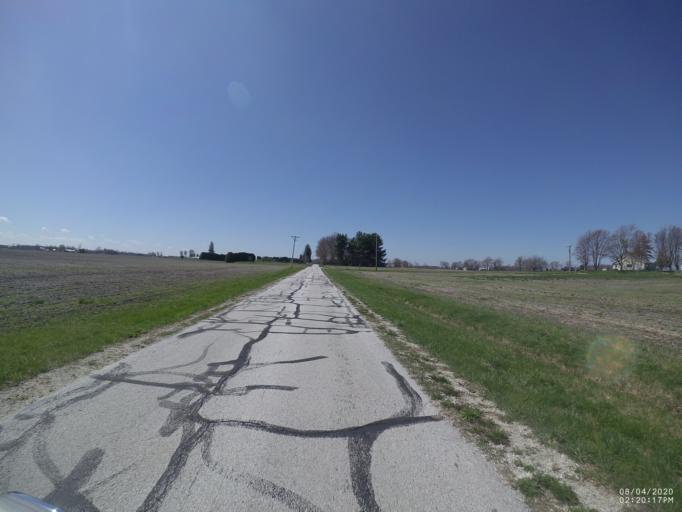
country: US
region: Ohio
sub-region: Sandusky County
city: Stony Prairie
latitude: 41.2894
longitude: -83.2510
